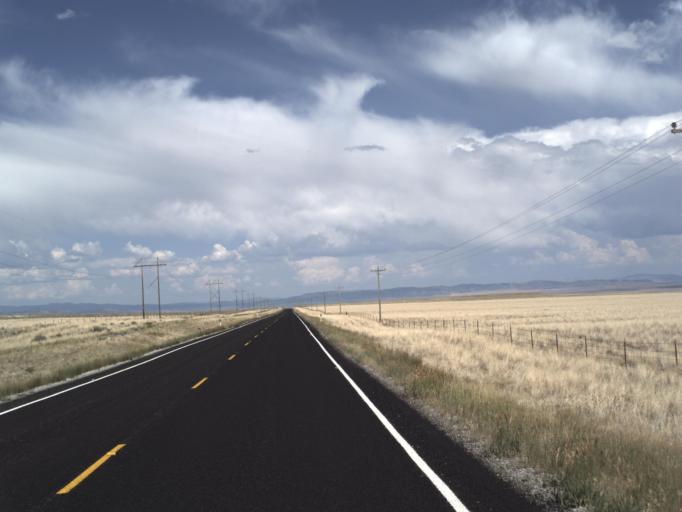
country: US
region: Idaho
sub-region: Power County
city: American Falls
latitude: 41.9674
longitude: -113.0853
